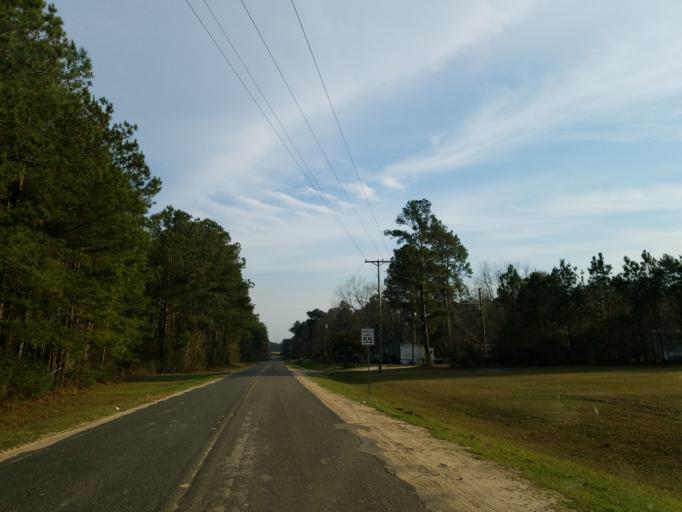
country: US
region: Georgia
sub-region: Tift County
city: Omega
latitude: 31.3914
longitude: -83.6353
